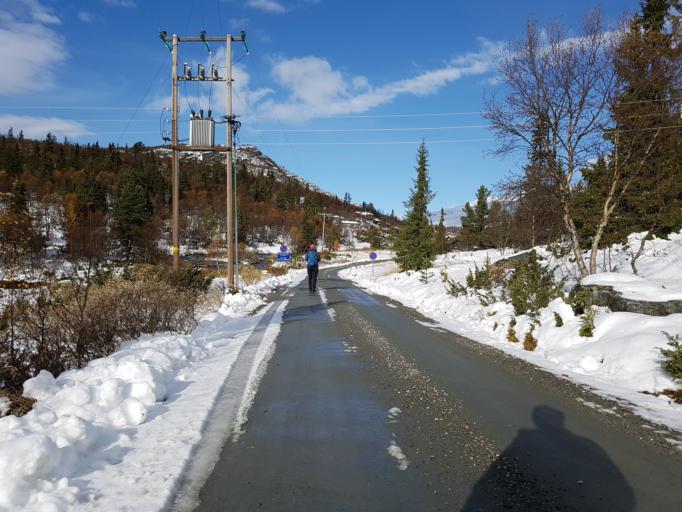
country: NO
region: Oppland
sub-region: Sel
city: Otta
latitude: 61.8163
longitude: 9.6780
